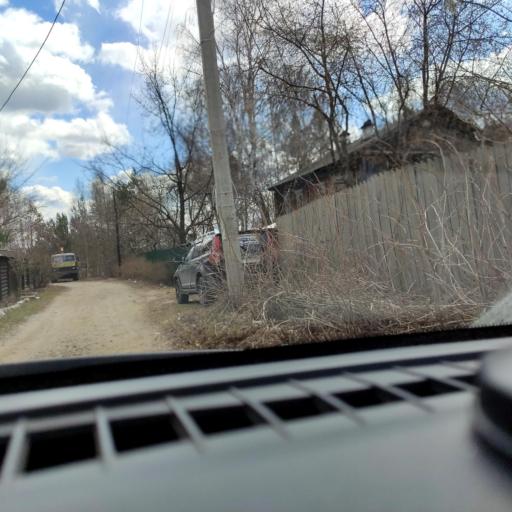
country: RU
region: Perm
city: Perm
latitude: 58.0513
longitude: 56.2966
